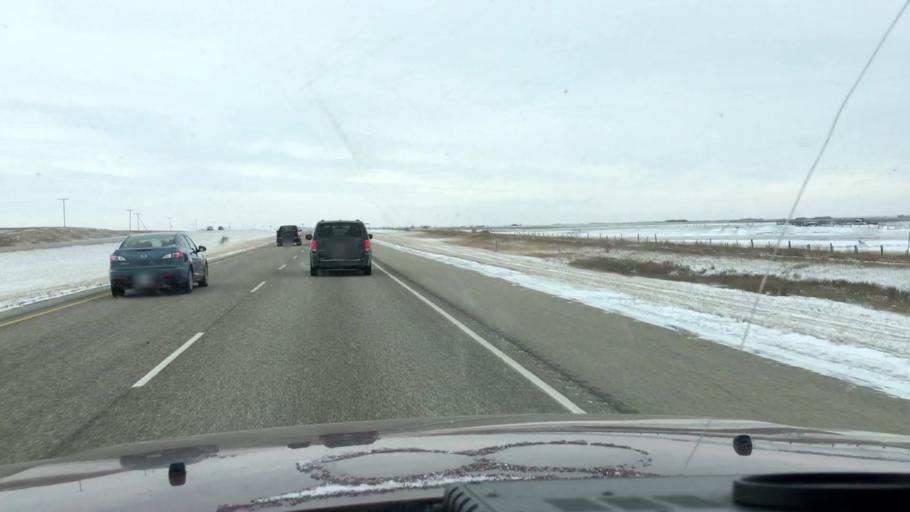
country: CA
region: Saskatchewan
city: Saskatoon
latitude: 51.5944
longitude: -106.3865
